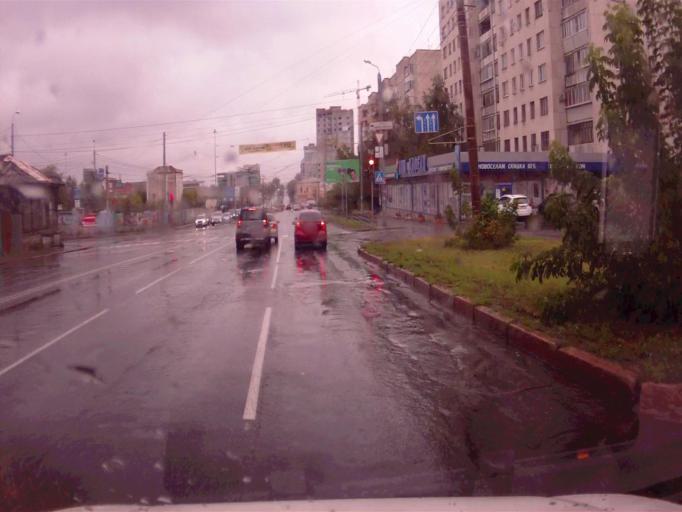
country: RU
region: Chelyabinsk
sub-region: Gorod Chelyabinsk
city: Chelyabinsk
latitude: 55.1652
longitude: 61.4161
